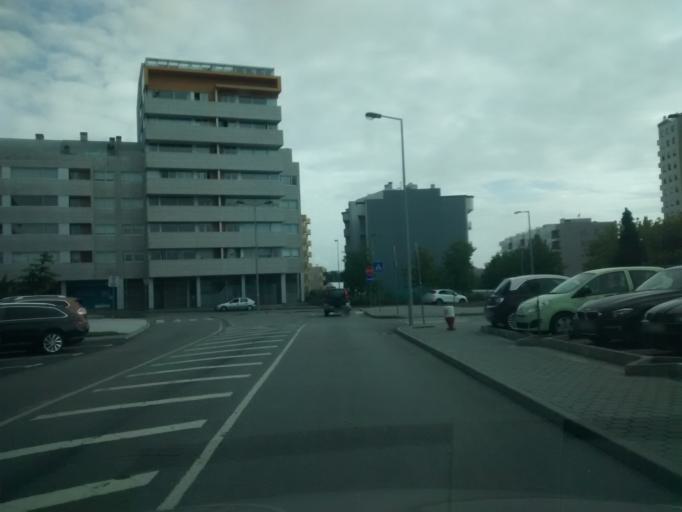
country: PT
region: Aveiro
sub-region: Aveiro
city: Aveiro
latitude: 40.6413
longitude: -8.6393
